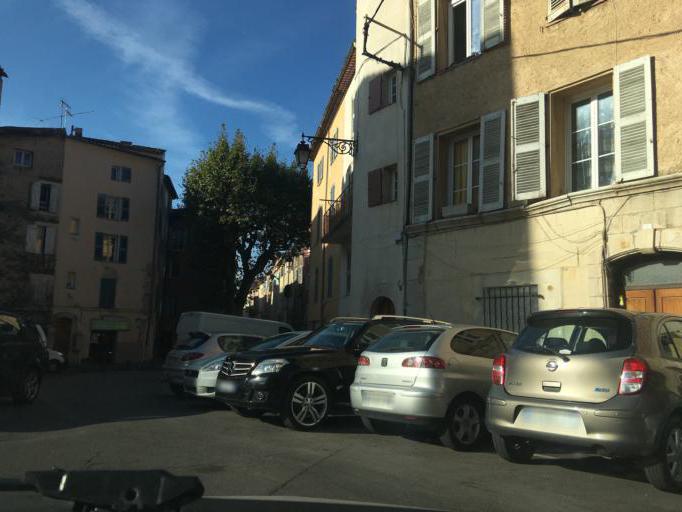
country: FR
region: Provence-Alpes-Cote d'Azur
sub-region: Departement du Var
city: Draguignan
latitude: 43.5411
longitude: 6.4656
